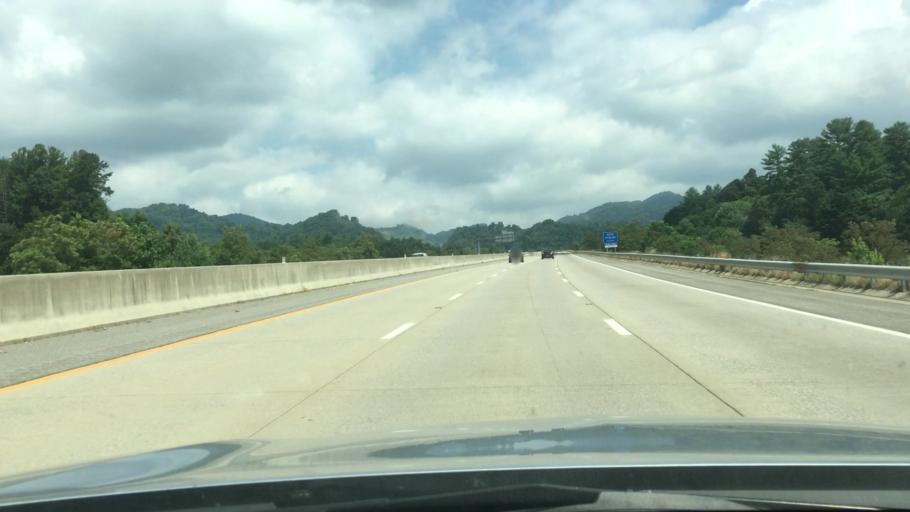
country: US
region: North Carolina
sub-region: Madison County
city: Mars Hill
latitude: 35.8541
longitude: -82.5292
